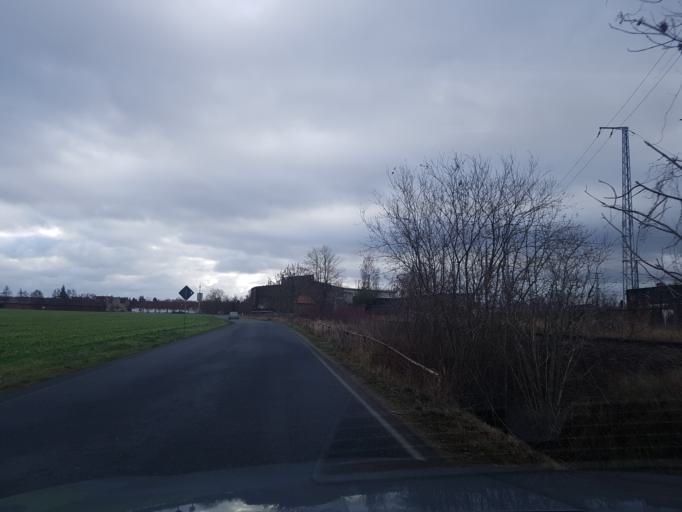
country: DE
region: Brandenburg
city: Falkenberg
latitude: 51.5917
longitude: 13.2456
